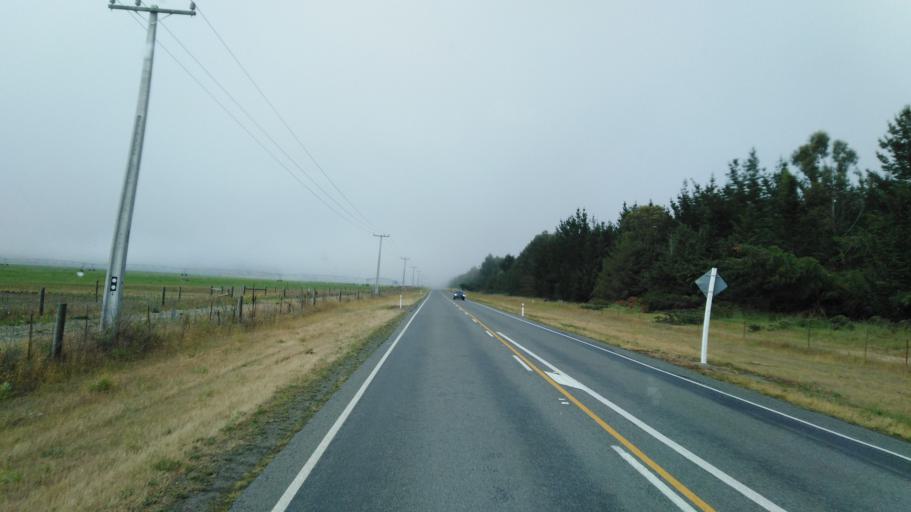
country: NZ
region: Canterbury
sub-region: Hurunui District
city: Amberley
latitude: -42.8187
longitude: 172.8124
